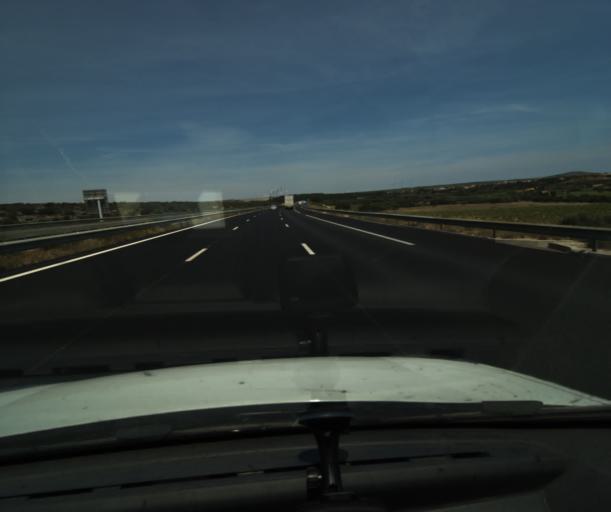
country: FR
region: Languedoc-Roussillon
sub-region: Departement de l'Aude
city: Sigean
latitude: 42.9702
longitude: 2.9698
